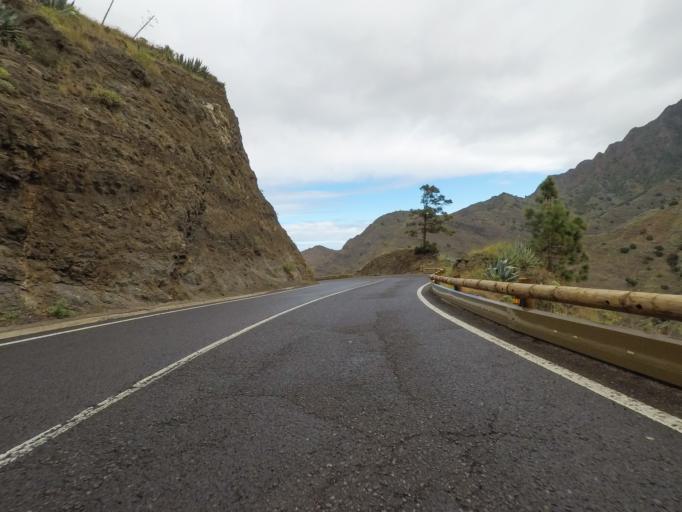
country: ES
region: Canary Islands
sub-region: Provincia de Santa Cruz de Tenerife
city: Hermigua
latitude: 28.1451
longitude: -17.1996
